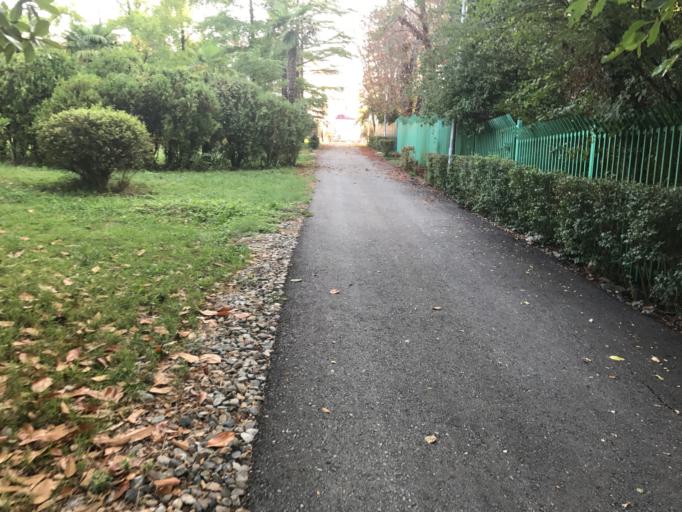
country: RU
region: Krasnodarskiy
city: Shepsi
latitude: 44.0067
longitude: 39.1817
